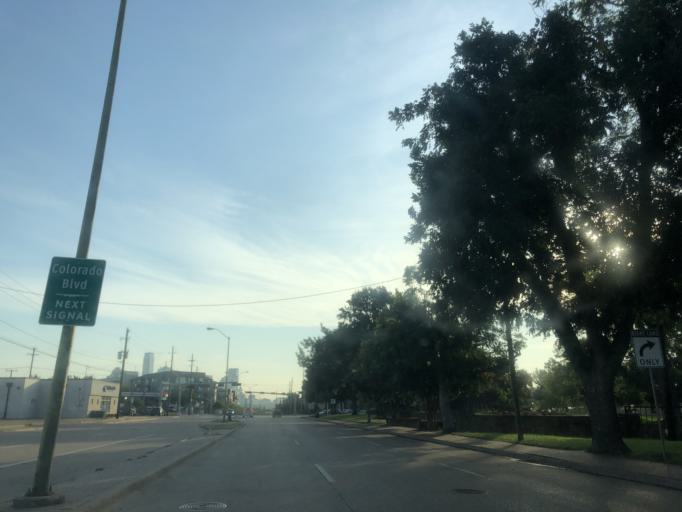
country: US
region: Texas
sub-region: Dallas County
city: Dallas
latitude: 32.7575
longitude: -96.8216
